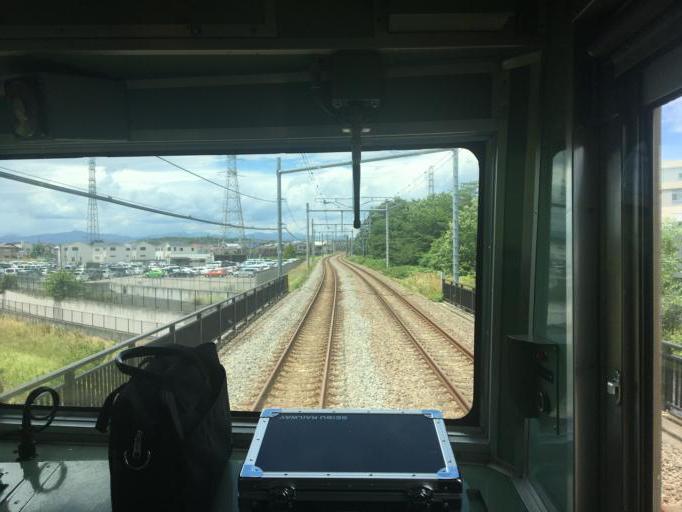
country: JP
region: Tokyo
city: Higashimurayama-shi
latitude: 35.7506
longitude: 139.4545
